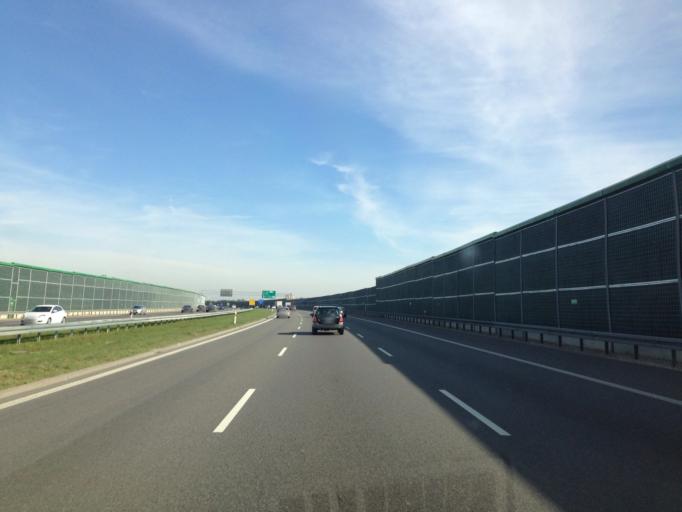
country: PL
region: Masovian Voivodeship
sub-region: Powiat pruszkowski
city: Pruszkow
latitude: 52.1927
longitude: 20.8121
